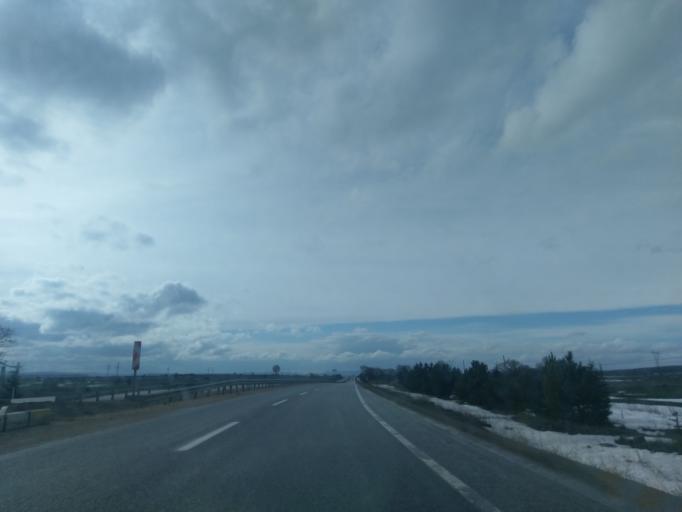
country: TR
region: Eskisehir
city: Inonu
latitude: 39.7206
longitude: 30.2269
